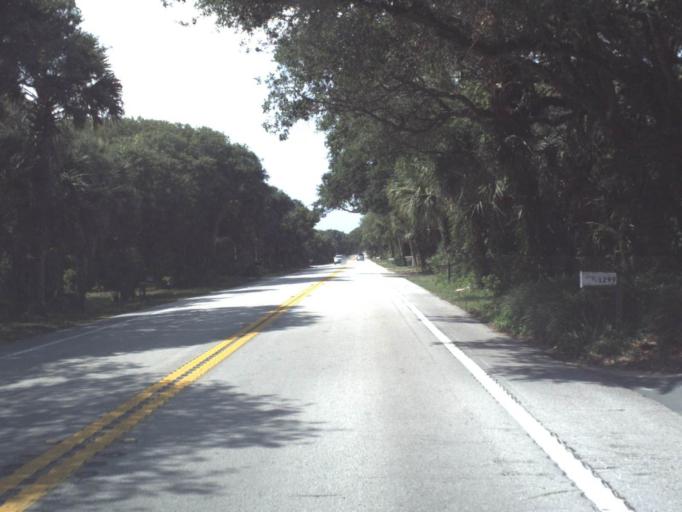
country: US
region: Florida
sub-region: Saint Johns County
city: Palm Valley
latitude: 30.1352
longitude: -81.3504
